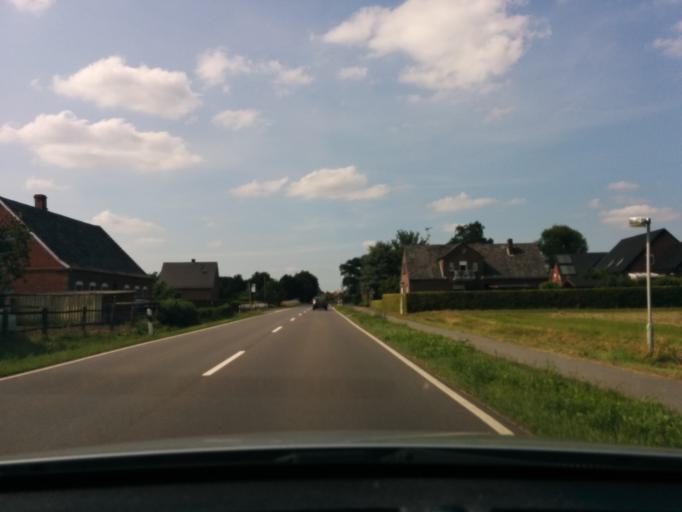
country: DE
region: North Rhine-Westphalia
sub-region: Regierungsbezirk Munster
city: Neuenkirchen
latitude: 52.2302
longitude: 7.3818
